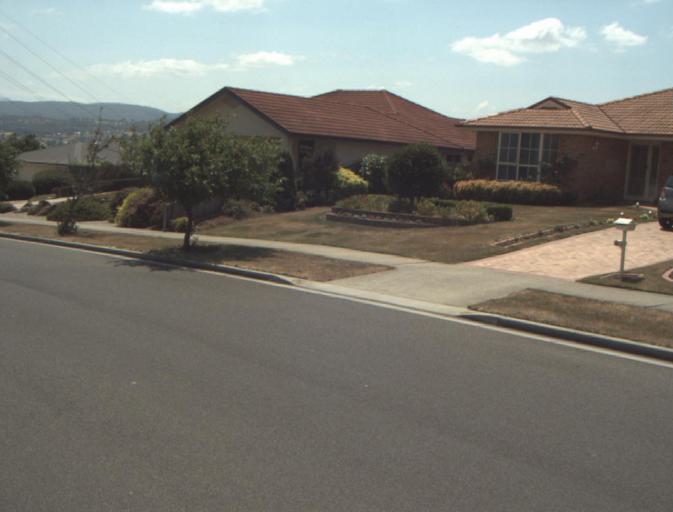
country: AU
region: Tasmania
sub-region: Launceston
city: Newstead
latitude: -41.4790
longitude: 147.1828
